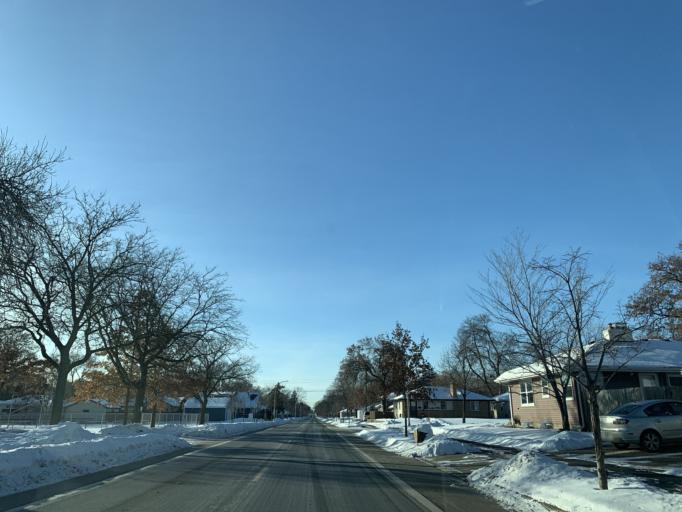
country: US
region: Minnesota
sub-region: Hennepin County
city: Richfield
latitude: 44.8656
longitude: -93.2498
